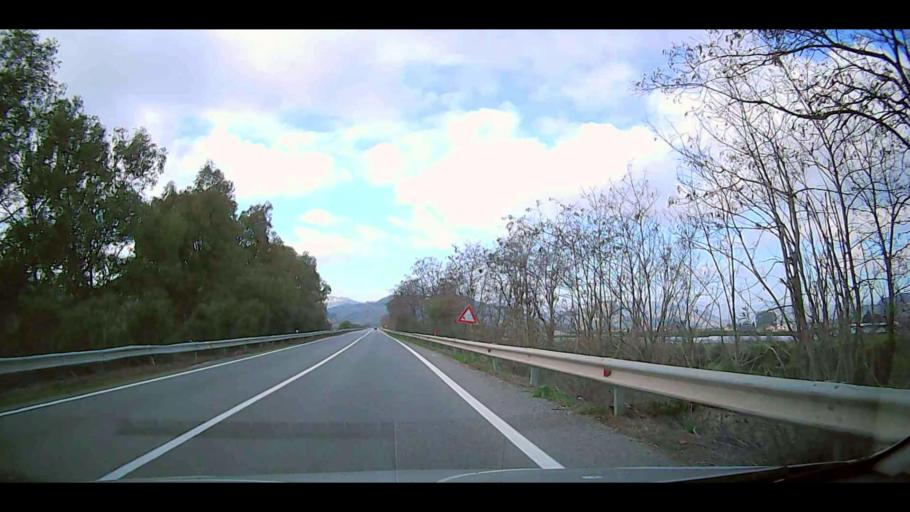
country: IT
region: Calabria
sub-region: Provincia di Crotone
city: Rocca di Neto
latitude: 39.1685
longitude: 16.9654
